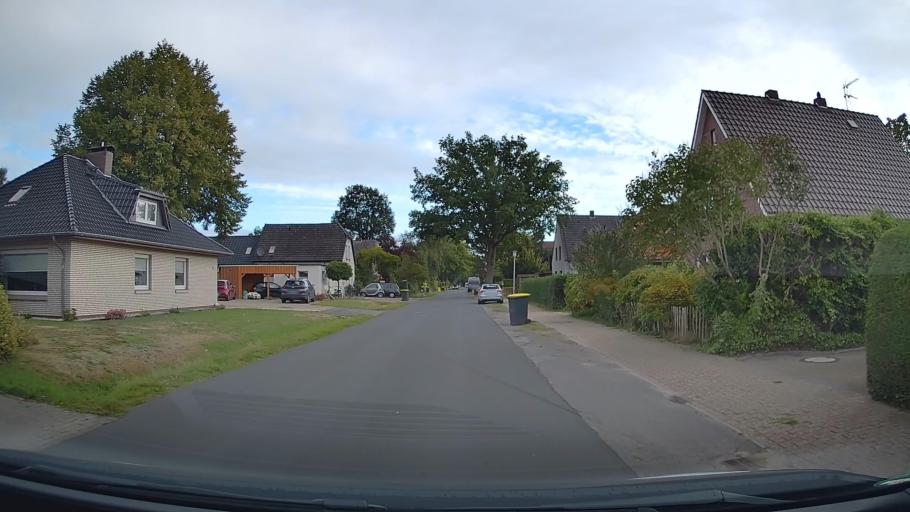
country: DE
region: Lower Saxony
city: Oldenburg
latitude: 53.1423
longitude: 8.1618
